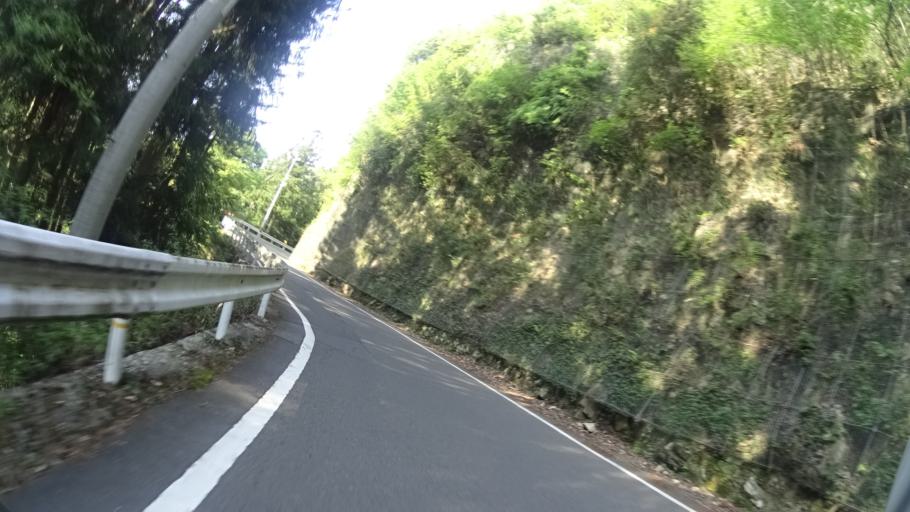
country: JP
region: Tokushima
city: Ikedacho
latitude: 33.9136
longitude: 133.8161
